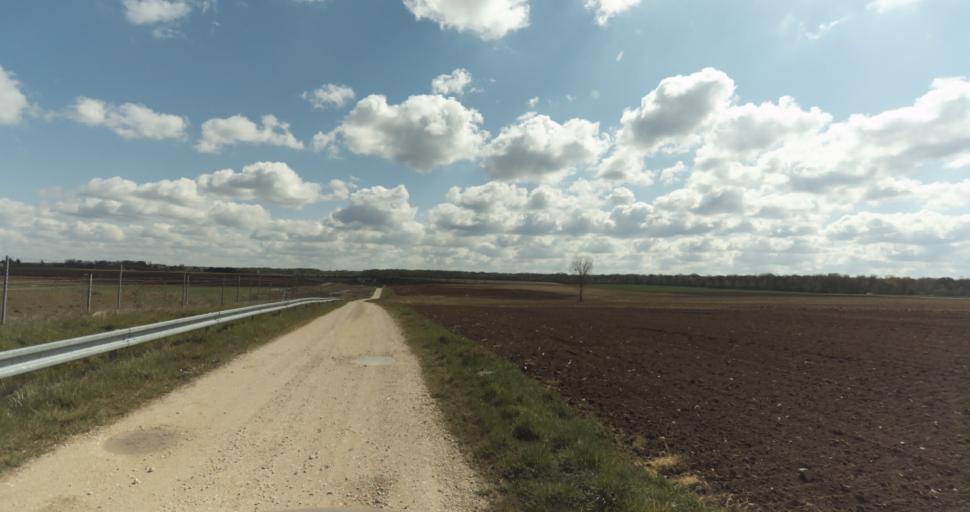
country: FR
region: Bourgogne
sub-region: Departement de la Cote-d'Or
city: Auxonne
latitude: 47.2223
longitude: 5.4301
